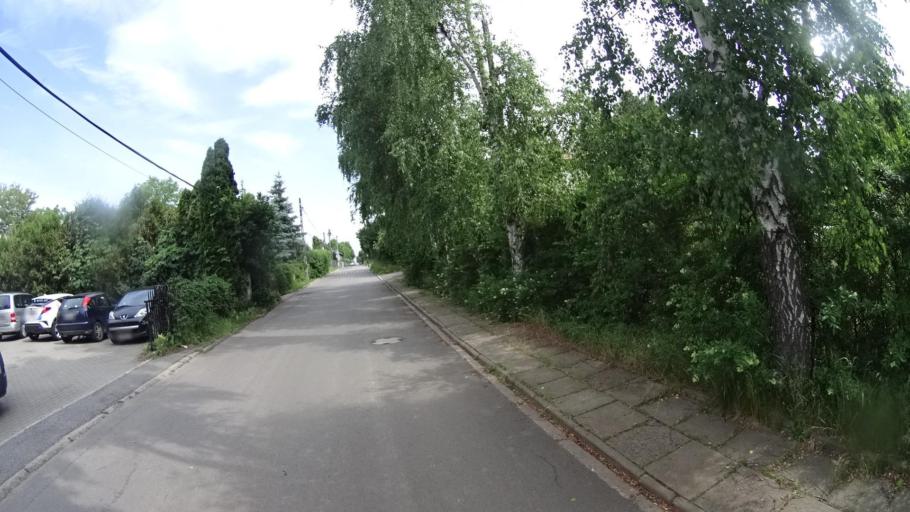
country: PL
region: Masovian Voivodeship
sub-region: Powiat pruszkowski
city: Raszyn
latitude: 52.1726
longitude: 20.9257
